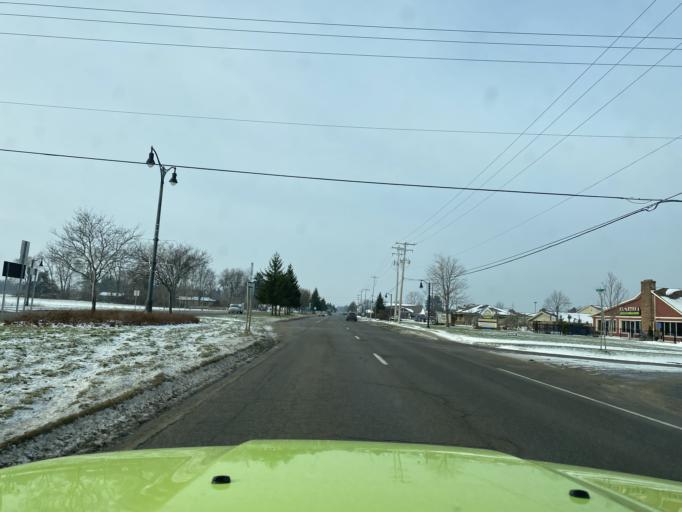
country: US
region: Michigan
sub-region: Ottawa County
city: Allendale
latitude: 42.9723
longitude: -85.9339
